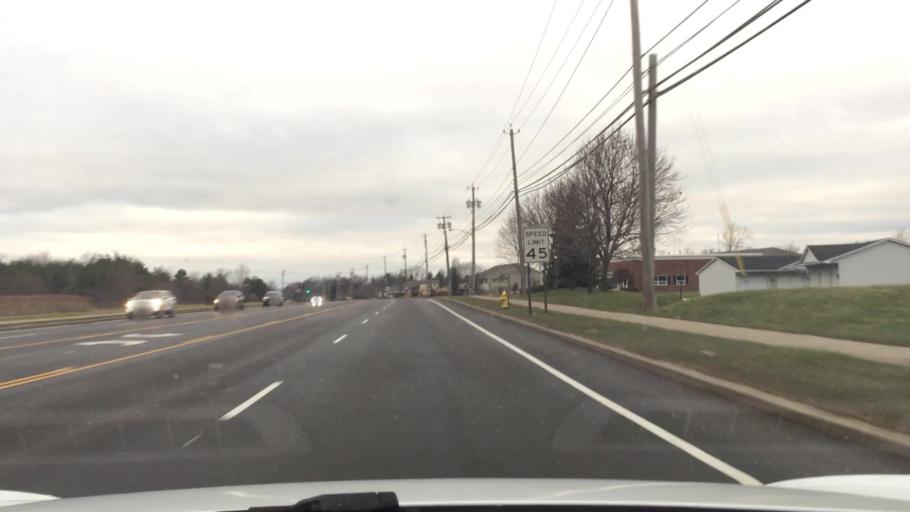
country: US
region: New York
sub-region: Erie County
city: Williamsville
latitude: 42.9782
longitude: -78.7259
